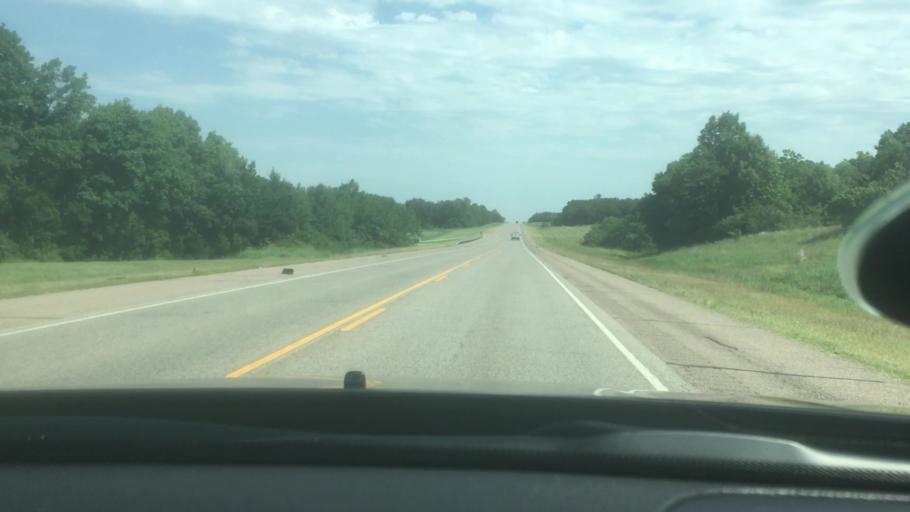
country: US
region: Oklahoma
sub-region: Seminole County
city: Konawa
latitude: 35.0019
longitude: -96.9314
